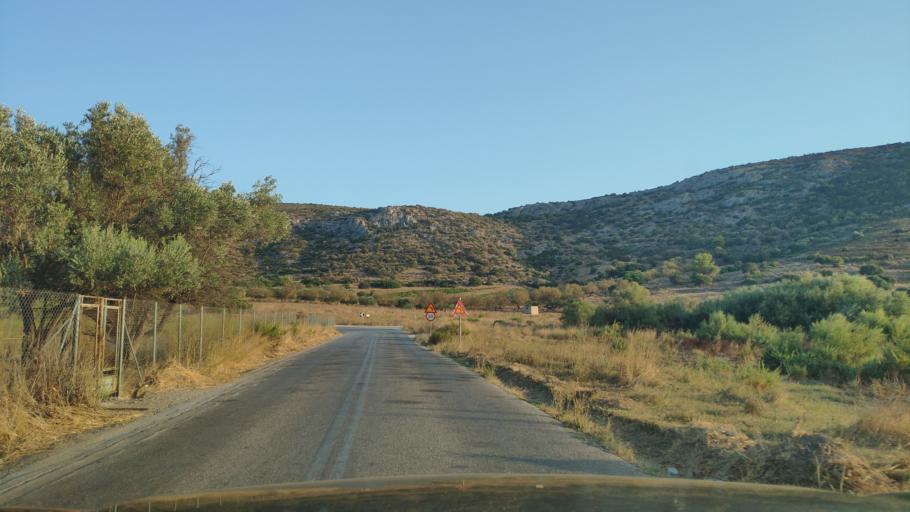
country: GR
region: Attica
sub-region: Nomarchia Anatolikis Attikis
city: Limin Mesoyaias
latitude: 37.9227
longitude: 23.9941
